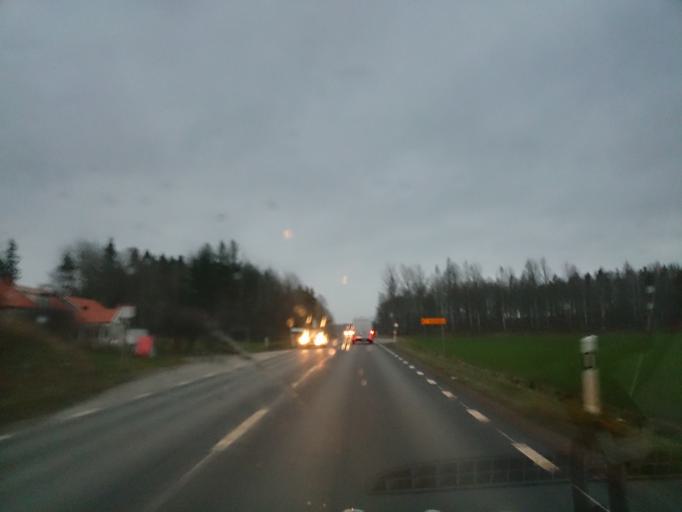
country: SE
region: OEstergoetland
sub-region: Linkopings Kommun
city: Linghem
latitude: 58.3806
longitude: 15.7960
